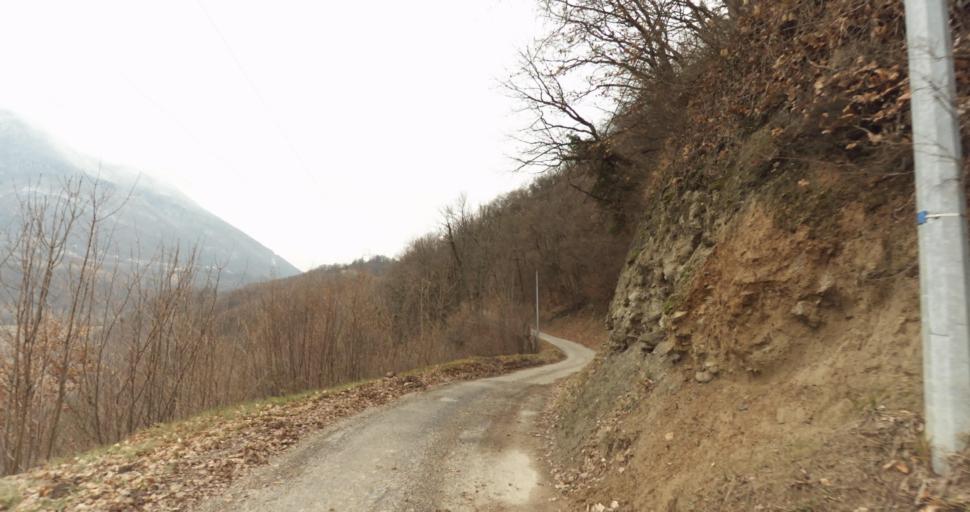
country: FR
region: Rhone-Alpes
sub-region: Departement de l'Isere
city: Saint-Georges-de-Commiers
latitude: 45.0315
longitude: 5.6902
